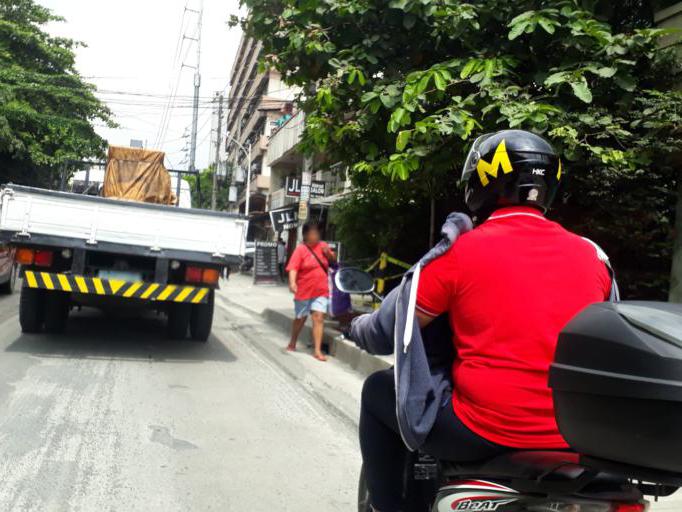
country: PH
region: Calabarzon
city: Bagong Pagasa
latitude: 14.6796
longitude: 121.0222
